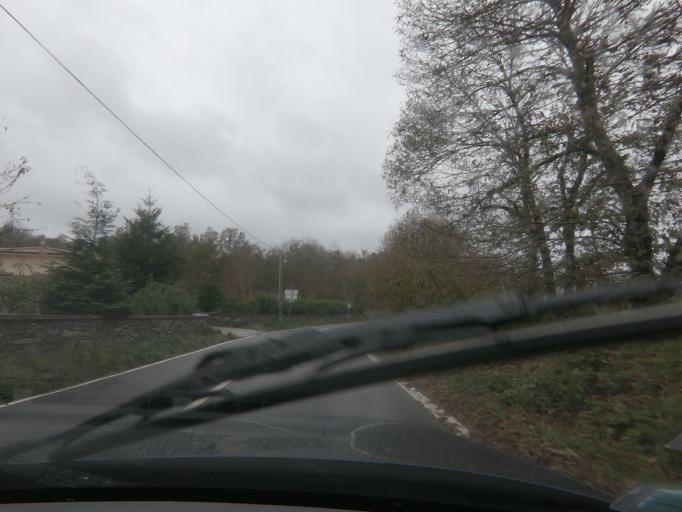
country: PT
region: Vila Real
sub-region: Santa Marta de Penaguiao
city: Santa Marta de Penaguiao
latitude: 41.2838
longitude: -7.8586
